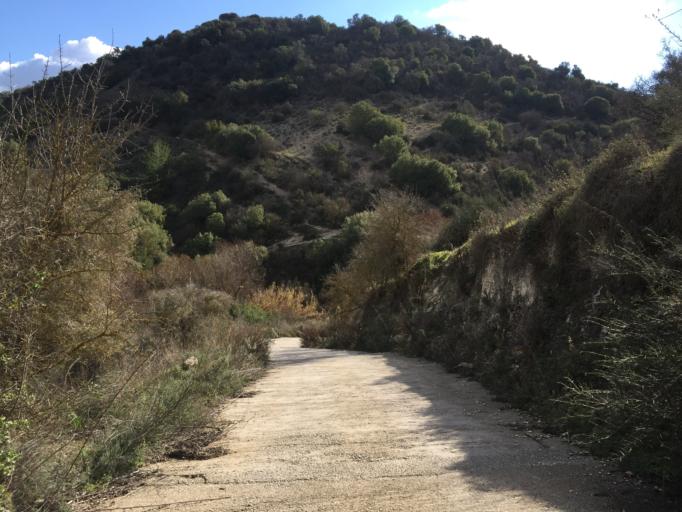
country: CY
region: Pafos
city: Mesogi
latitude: 34.8327
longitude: 32.5175
